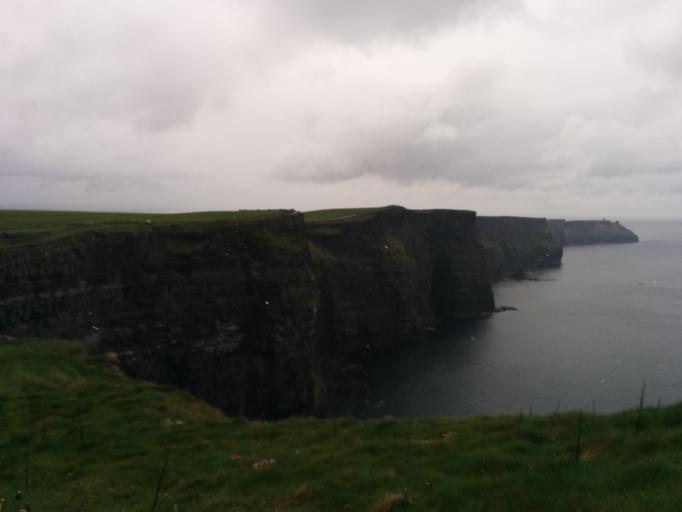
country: IE
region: Munster
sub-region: An Clar
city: Kilrush
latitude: 52.9721
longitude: -9.4292
